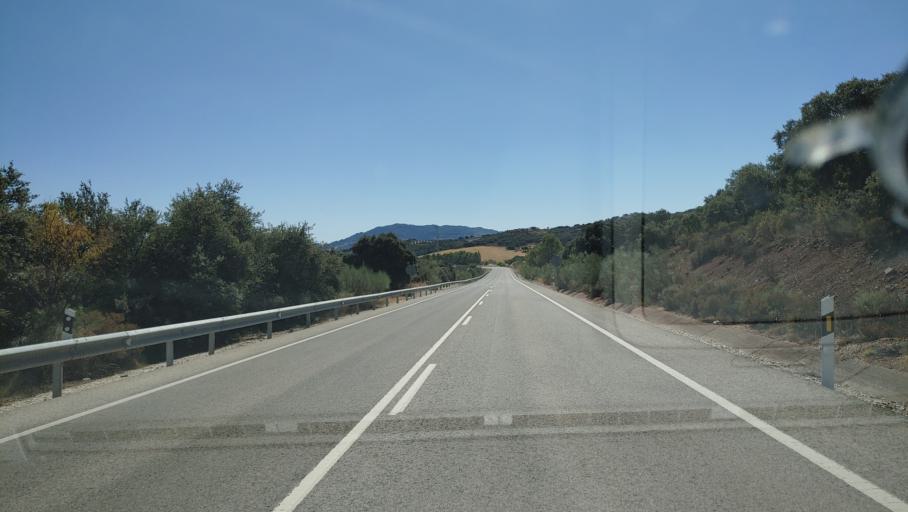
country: ES
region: Andalusia
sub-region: Provincia de Jaen
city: Genave
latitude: 38.4622
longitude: -2.7633
